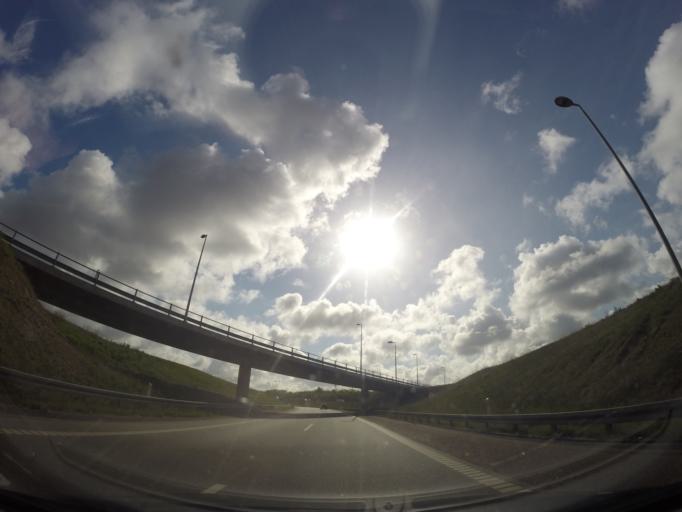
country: DK
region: Capital Region
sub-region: Glostrup Kommune
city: Glostrup
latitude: 55.6921
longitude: 12.4083
